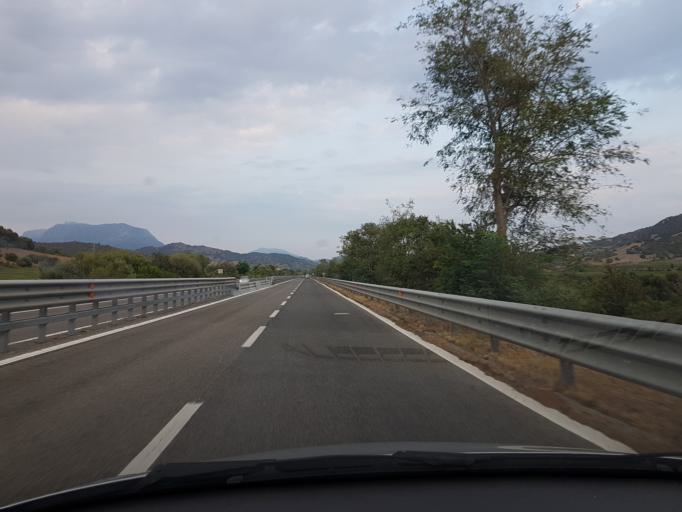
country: IT
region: Sardinia
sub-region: Provincia di Nuoro
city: Orune
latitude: 40.3819
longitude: 9.4370
